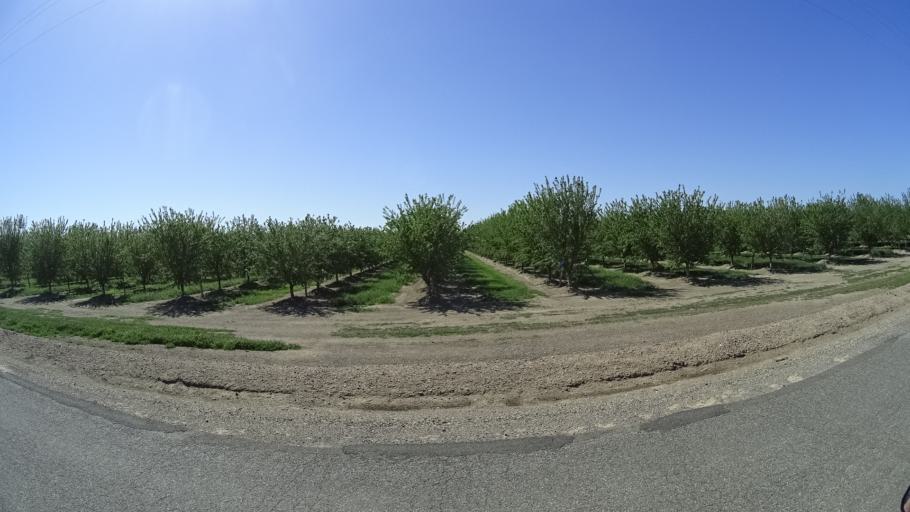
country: US
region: California
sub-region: Glenn County
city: Orland
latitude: 39.6972
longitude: -122.2444
